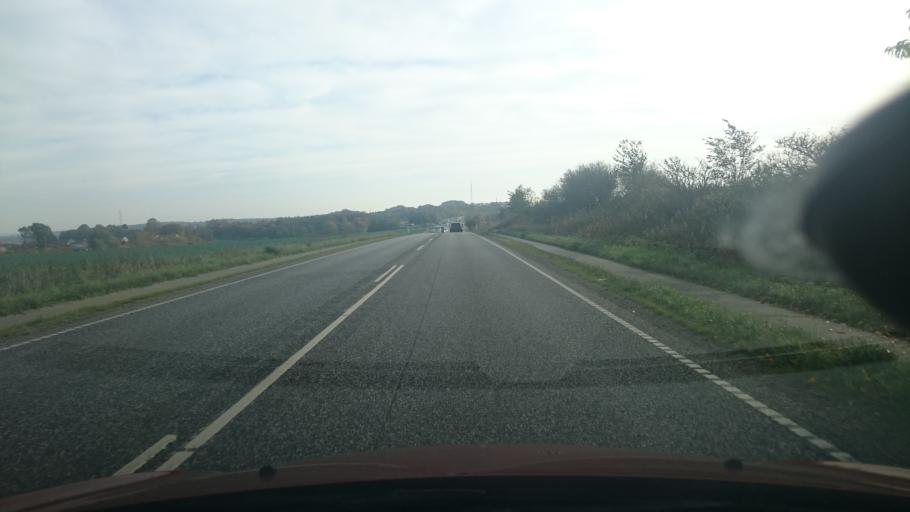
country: DK
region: Central Jutland
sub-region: Randers Kommune
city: Assentoft
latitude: 56.4411
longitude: 10.1069
